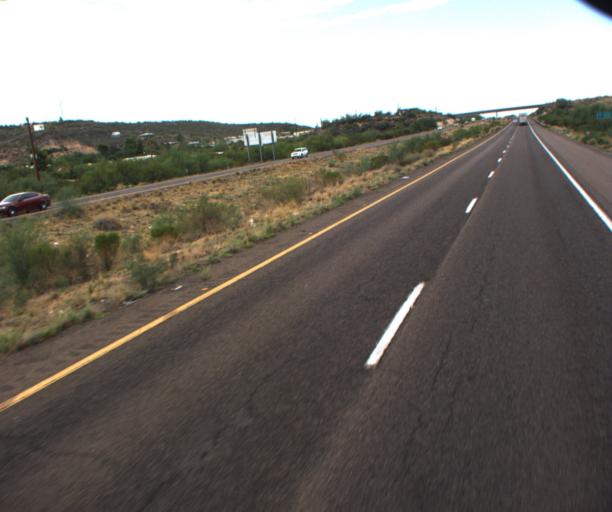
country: US
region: Arizona
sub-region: Yavapai County
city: Black Canyon City
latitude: 34.0695
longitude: -112.1415
